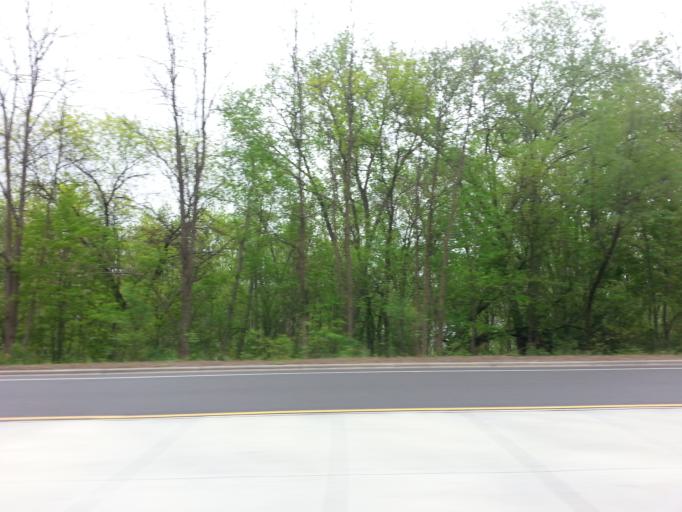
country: US
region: Minnesota
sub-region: Washington County
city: Oak Park Heights
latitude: 45.0450
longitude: -92.7964
